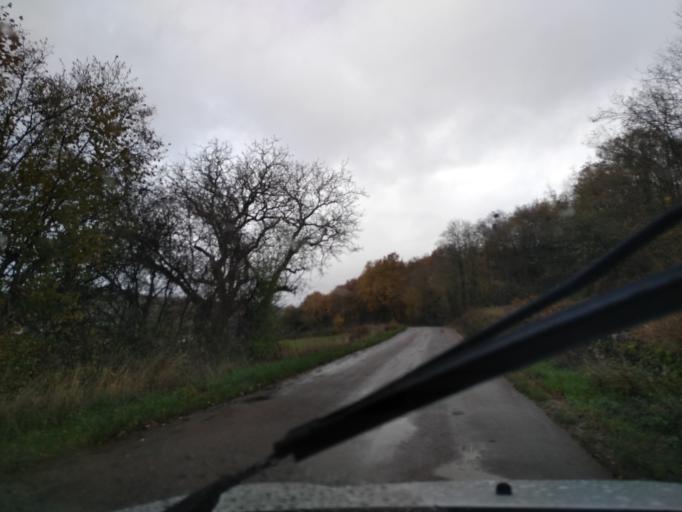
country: FR
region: Bourgogne
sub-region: Departement de Saone-et-Loire
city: Saint-Leger-sur-Dheune
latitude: 46.8609
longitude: 4.6863
